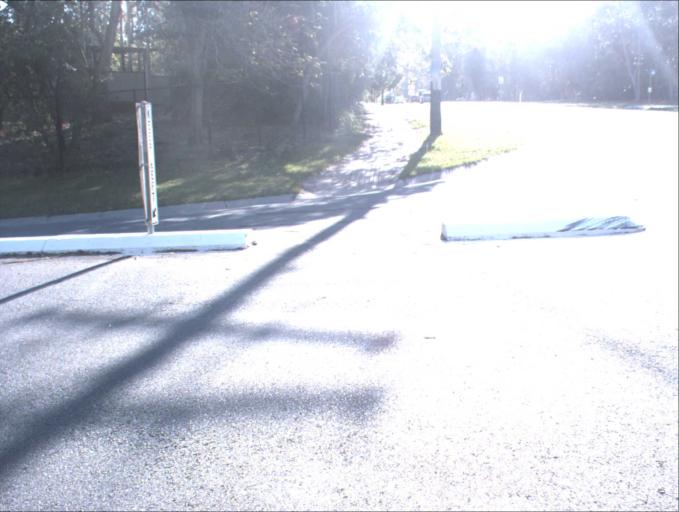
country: AU
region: Queensland
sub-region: Logan
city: Park Ridge South
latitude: -27.6988
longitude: 153.0235
